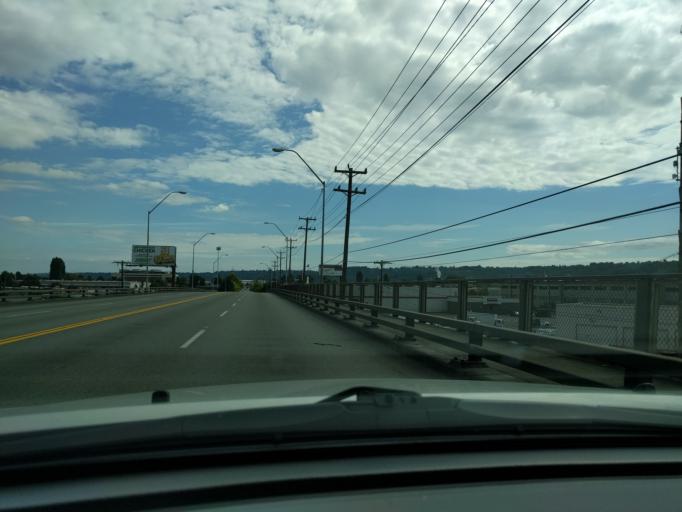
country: US
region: Washington
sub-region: King County
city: Seattle
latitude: 47.5595
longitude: -122.3295
